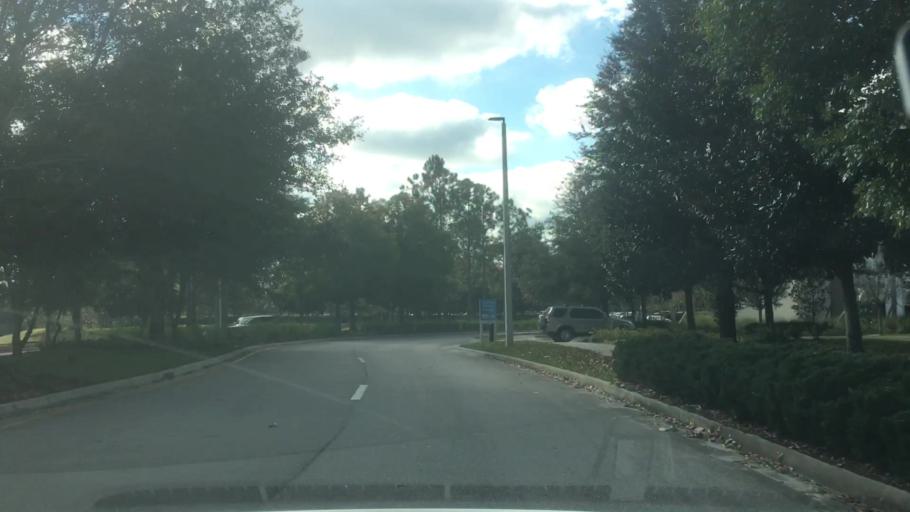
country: US
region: Florida
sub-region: Saint Johns County
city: Fruit Cove
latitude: 30.1401
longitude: -81.5332
